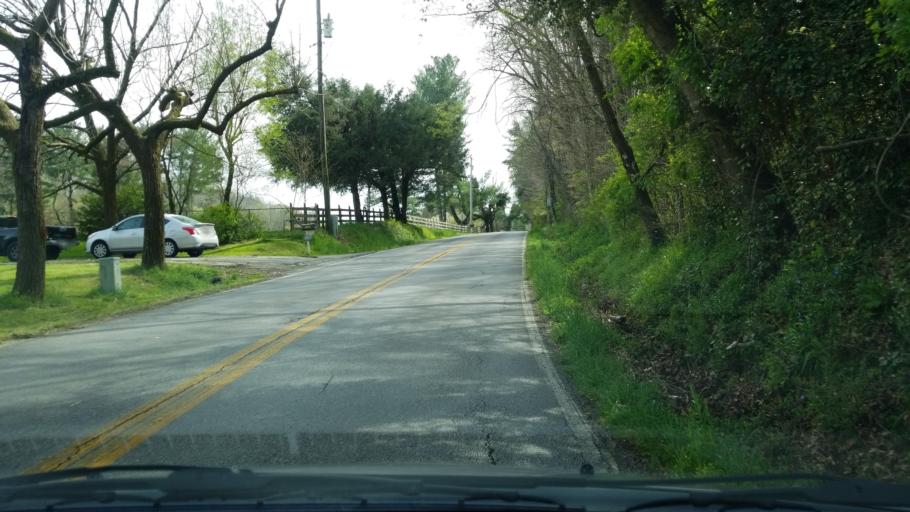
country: US
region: Tennessee
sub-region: Hamilton County
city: Falling Water
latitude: 35.1836
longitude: -85.2540
